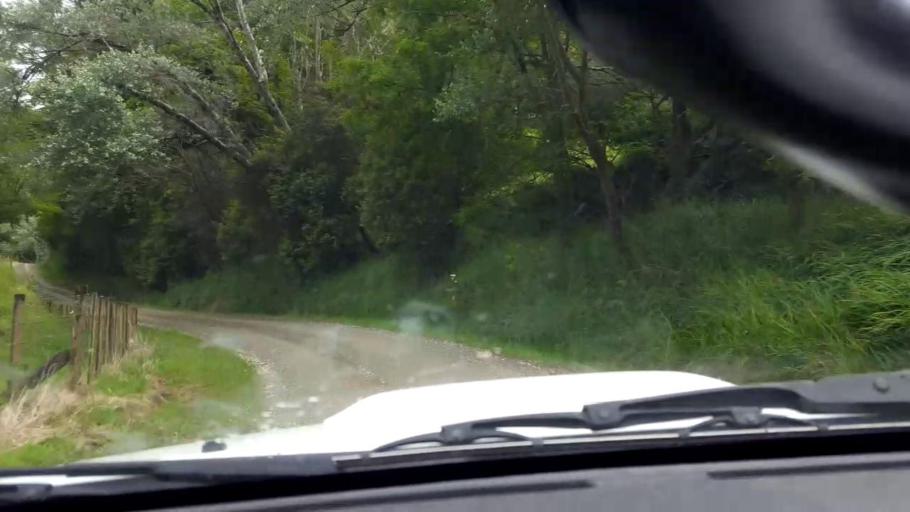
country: NZ
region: Gisborne
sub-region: Gisborne District
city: Gisborne
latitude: -38.3837
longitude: 177.6295
